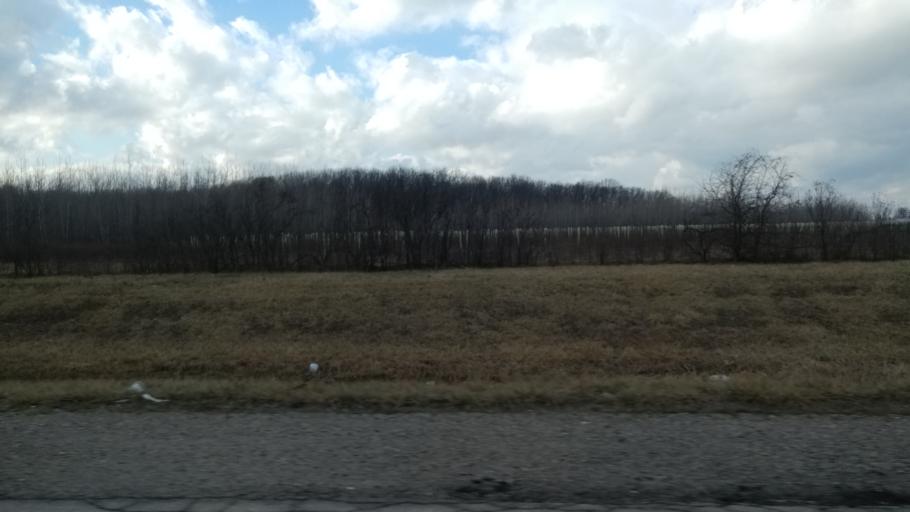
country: US
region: Ohio
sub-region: Lucas County
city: Maumee
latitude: 41.5513
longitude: -83.6896
